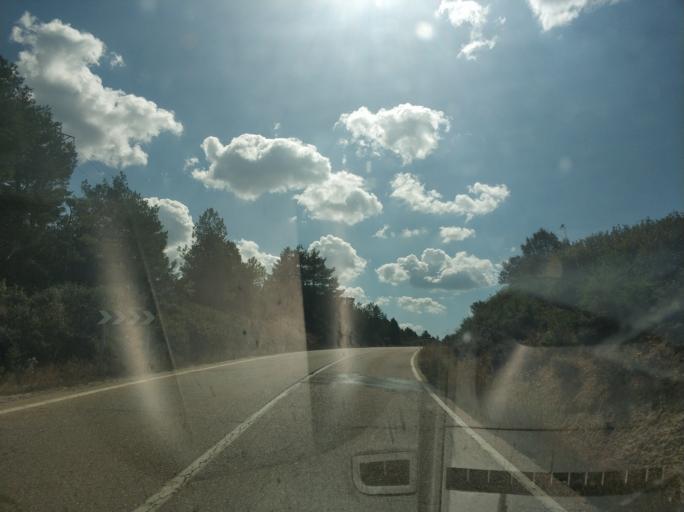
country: ES
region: Castille and Leon
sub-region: Provincia de Soria
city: Casarejos
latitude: 41.7790
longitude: -3.0268
